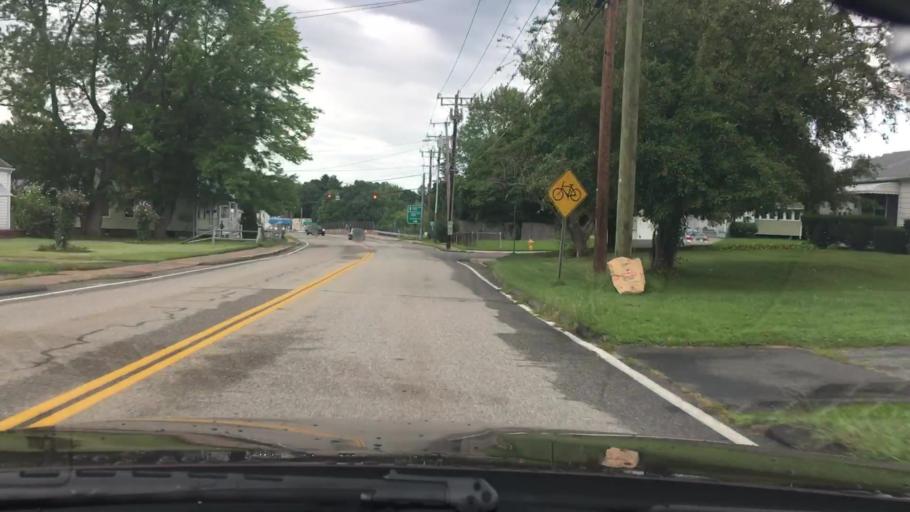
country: US
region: Connecticut
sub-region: Hartford County
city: Manchester
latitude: 41.7616
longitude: -72.5417
